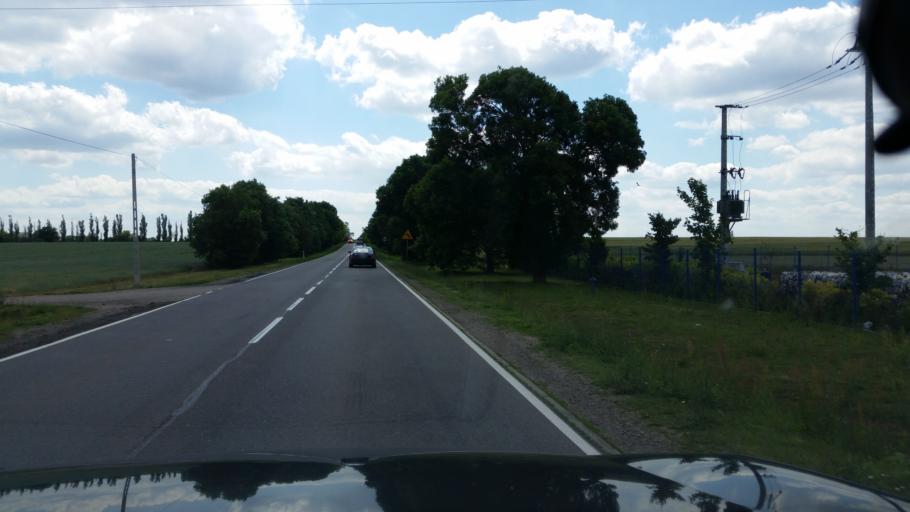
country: PL
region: Masovian Voivodeship
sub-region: Powiat ostrowski
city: Ostrow Mazowiecka
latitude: 52.8480
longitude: 21.8684
